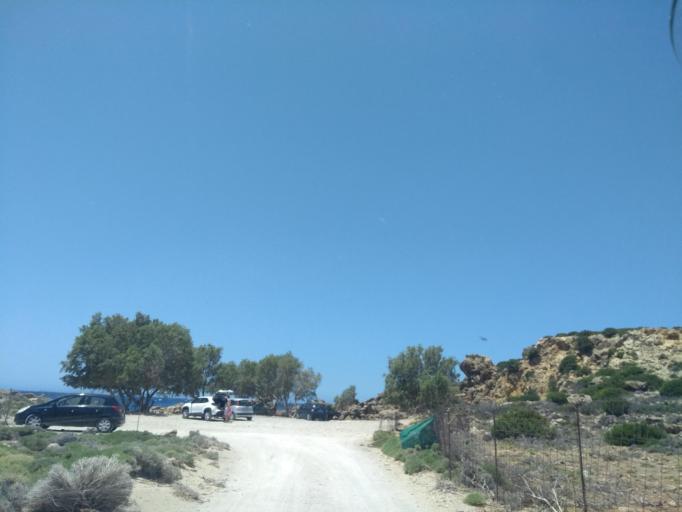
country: GR
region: Crete
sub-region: Nomos Chanias
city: Vryses
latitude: 35.3148
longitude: 23.5345
